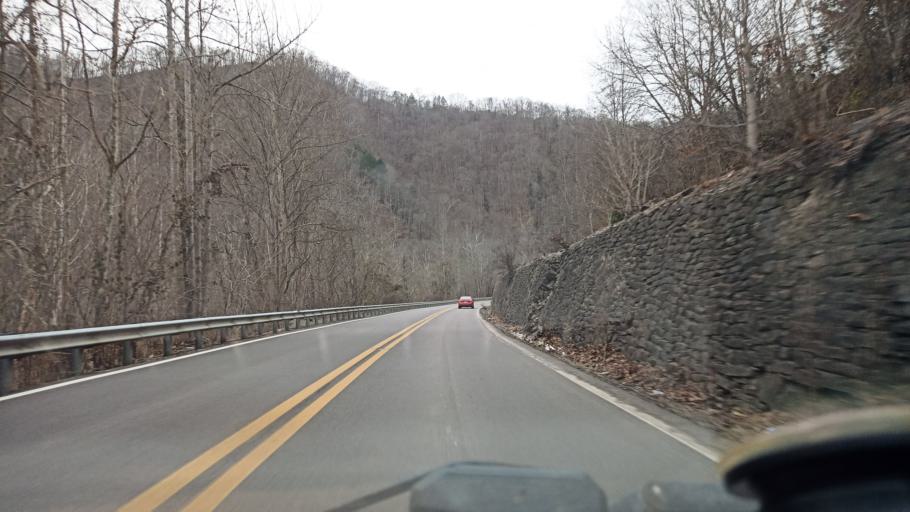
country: US
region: West Virginia
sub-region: Logan County
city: Mallory
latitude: 37.6927
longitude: -81.8682
